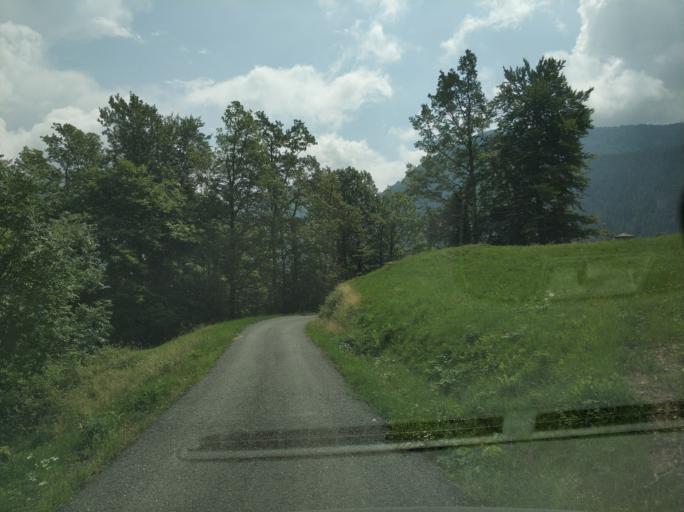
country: IT
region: Piedmont
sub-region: Provincia di Torino
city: Viu
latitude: 45.1984
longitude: 7.3844
